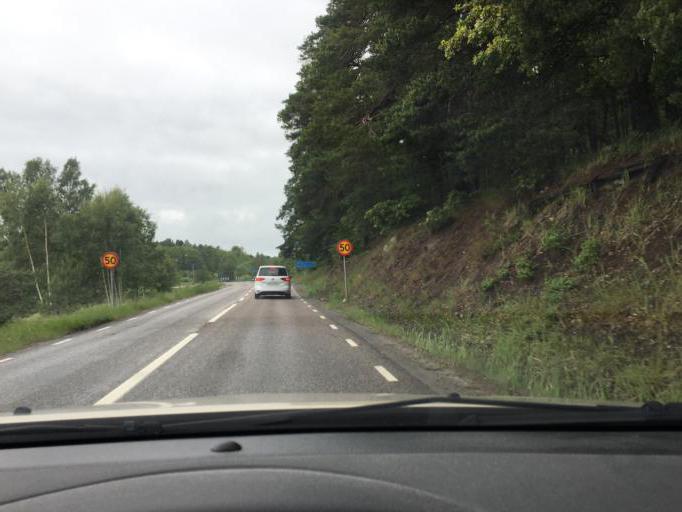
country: SE
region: Stockholm
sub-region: Varmdo Kommun
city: Hemmesta
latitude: 59.3274
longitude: 18.5071
